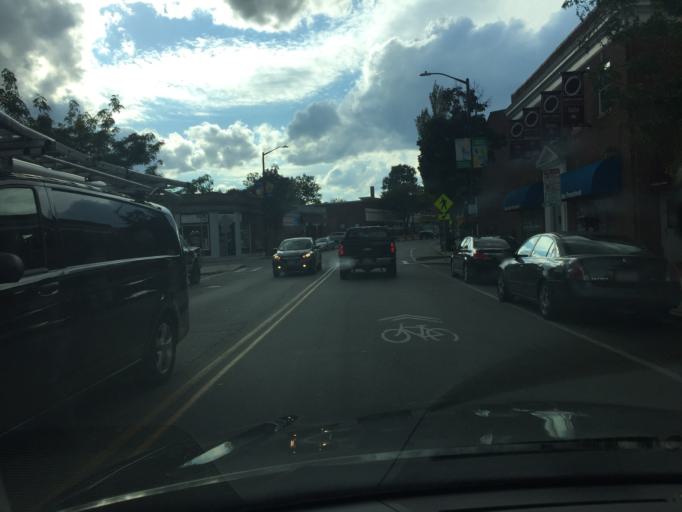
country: US
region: Massachusetts
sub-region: Middlesex County
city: Medford
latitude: 42.4212
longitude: -71.1304
